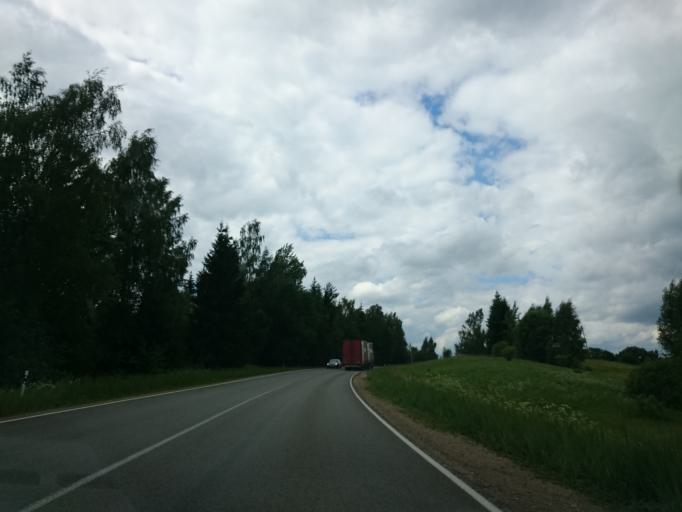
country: LV
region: Ludzas Rajons
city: Ludza
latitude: 56.5343
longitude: 27.5832
